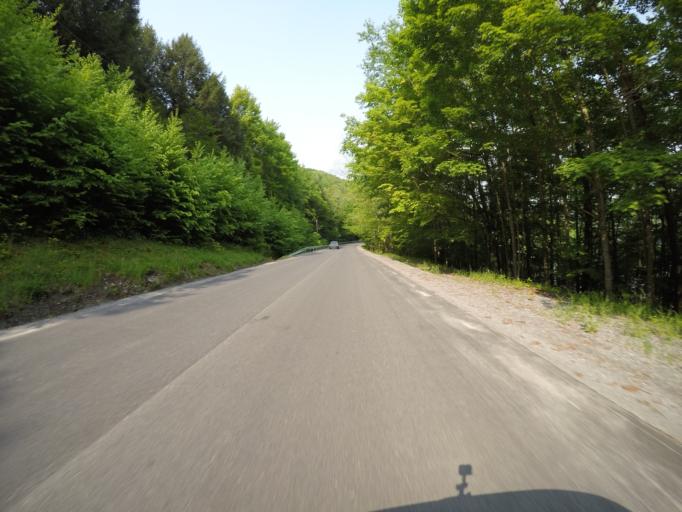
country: US
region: New York
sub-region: Sullivan County
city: Livingston Manor
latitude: 42.1213
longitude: -74.7027
